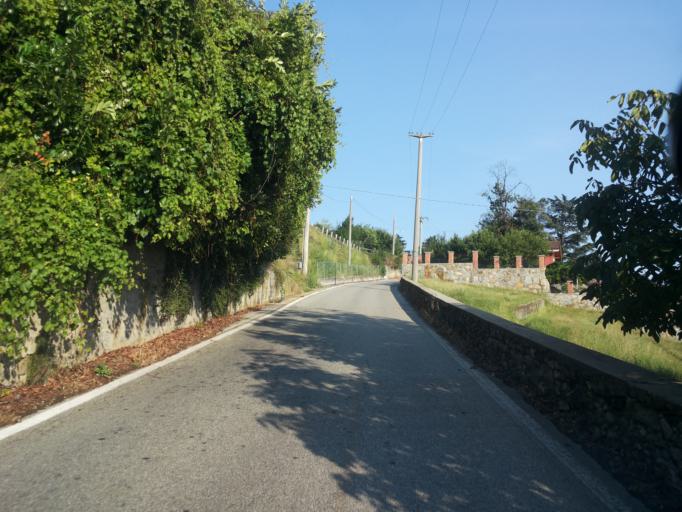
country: IT
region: Piedmont
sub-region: Provincia di Torino
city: Piverone
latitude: 45.4520
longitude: 7.9988
